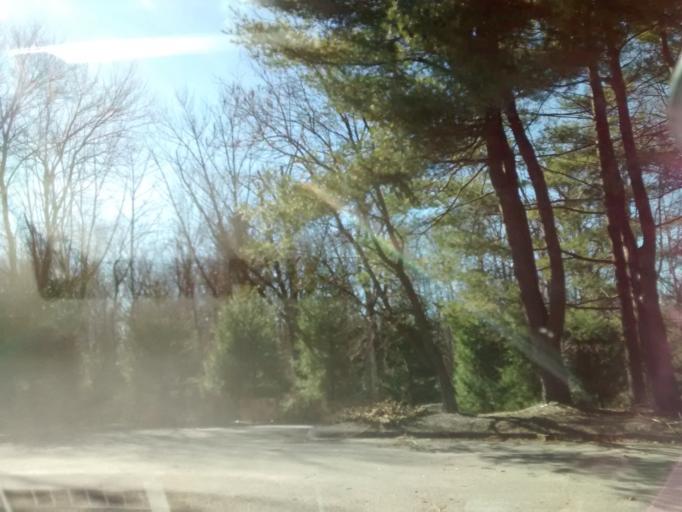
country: US
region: Massachusetts
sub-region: Worcester County
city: Worcester
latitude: 42.2913
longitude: -71.8225
